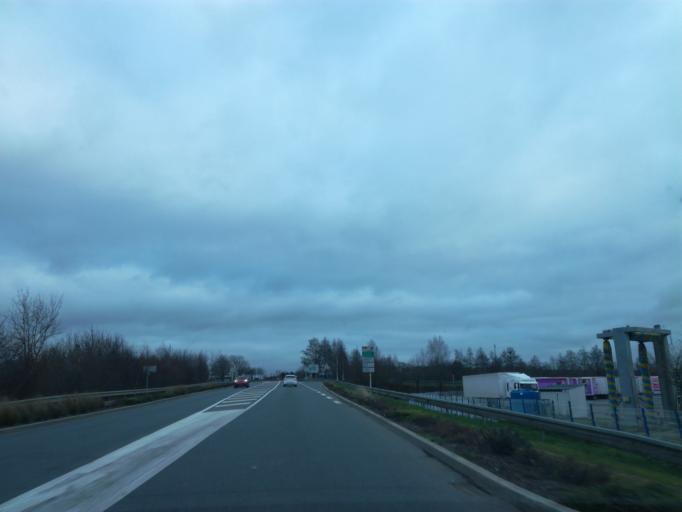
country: FR
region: Brittany
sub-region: Departement du Morbihan
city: Saint-Thuriau
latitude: 48.0412
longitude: -2.9527
